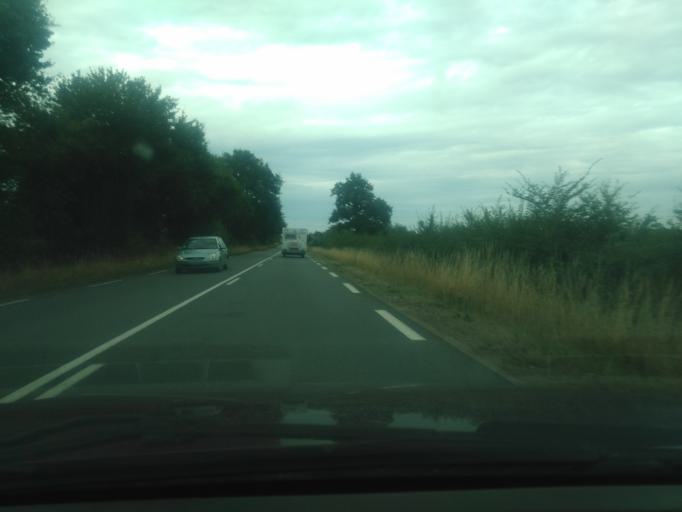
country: FR
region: Centre
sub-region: Departement du Cher
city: Sancoins
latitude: 46.8192
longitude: 2.9151
